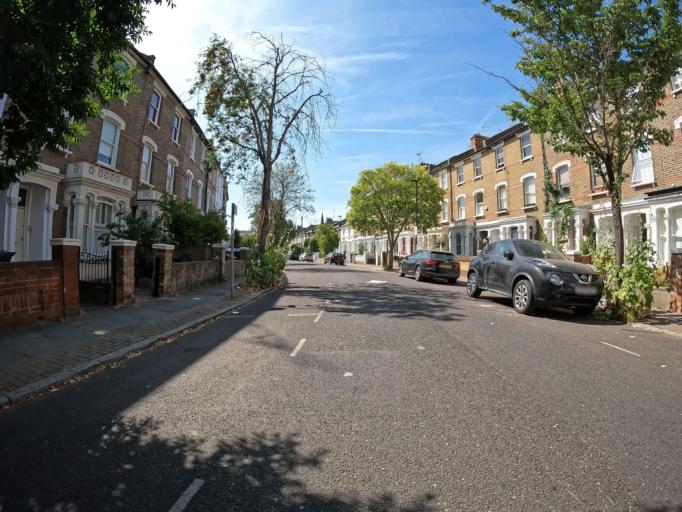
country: GB
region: England
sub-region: Greater London
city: Harringay
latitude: 51.5613
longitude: -0.1037
